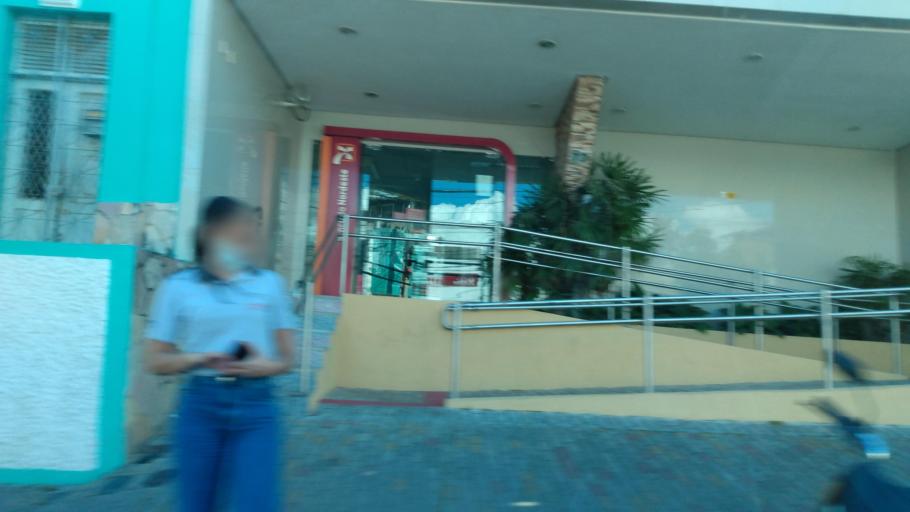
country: ET
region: Oromiya
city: Gore
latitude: 8.2011
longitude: 35.5658
